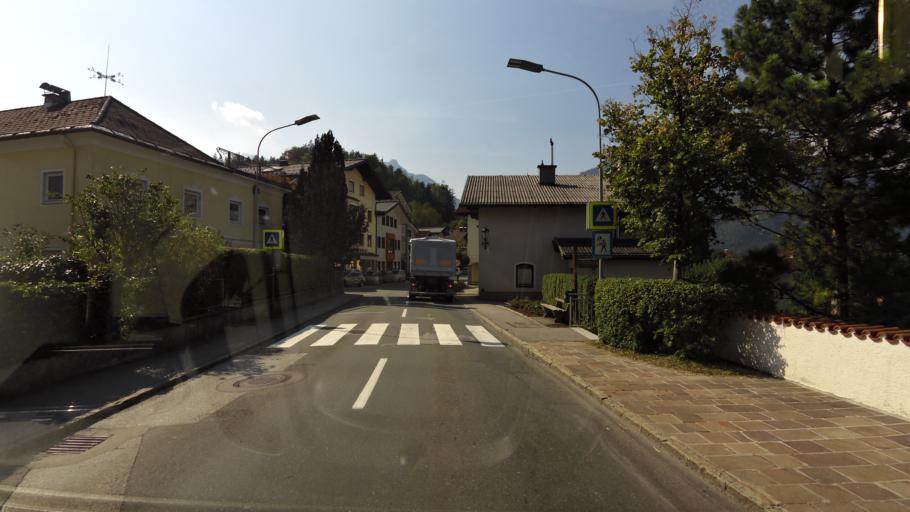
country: AT
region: Salzburg
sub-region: Politischer Bezirk Hallein
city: Golling an der Salzach
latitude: 47.6004
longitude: 13.1683
